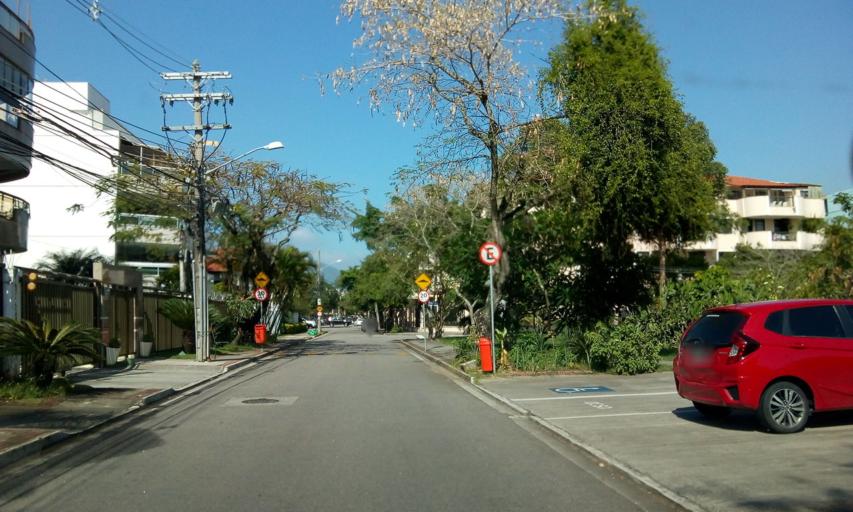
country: BR
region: Rio de Janeiro
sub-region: Nilopolis
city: Nilopolis
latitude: -23.0172
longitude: -43.4556
